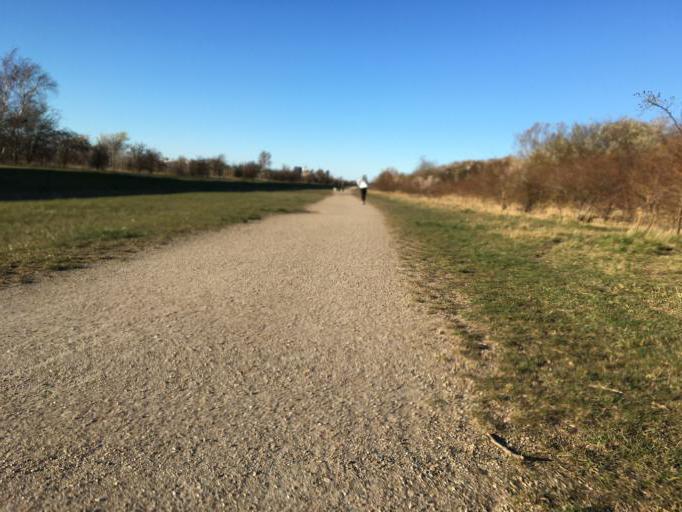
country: DK
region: Capital Region
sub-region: Tarnby Kommune
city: Tarnby
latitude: 55.5967
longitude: 12.5733
